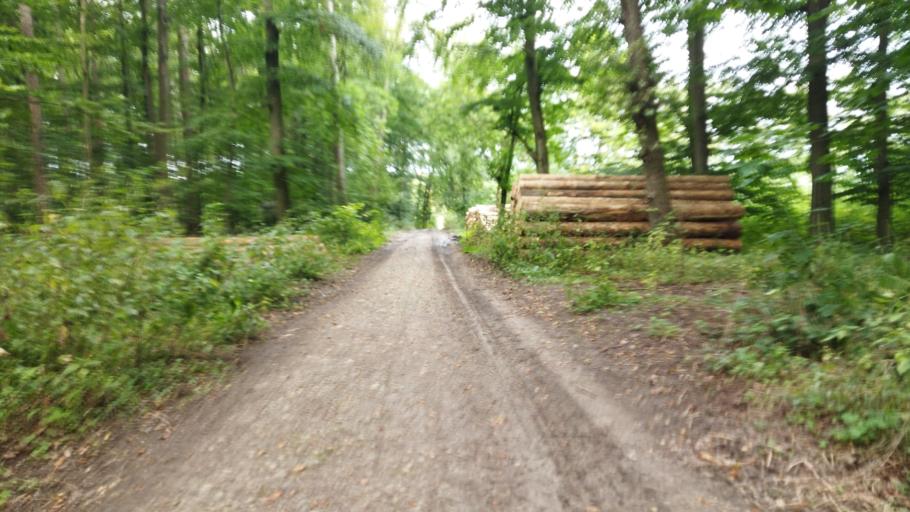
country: DE
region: Lower Saxony
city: Hilter
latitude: 52.1222
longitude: 8.1491
